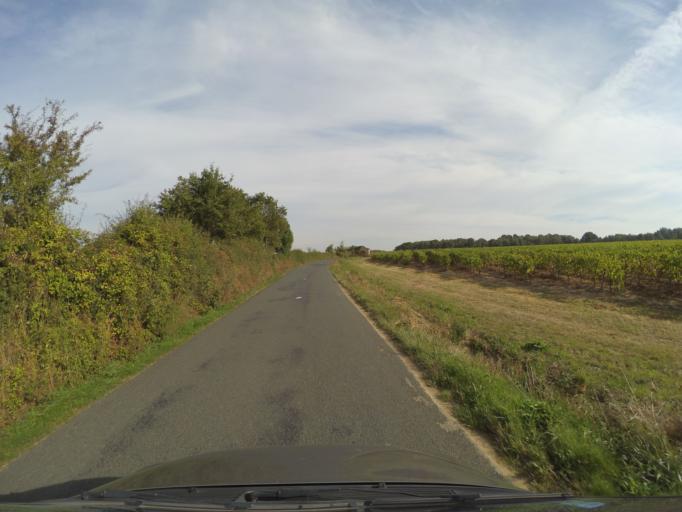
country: FR
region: Pays de la Loire
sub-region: Departement de Maine-et-Loire
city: Tillieres
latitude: 47.1591
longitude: -1.1427
